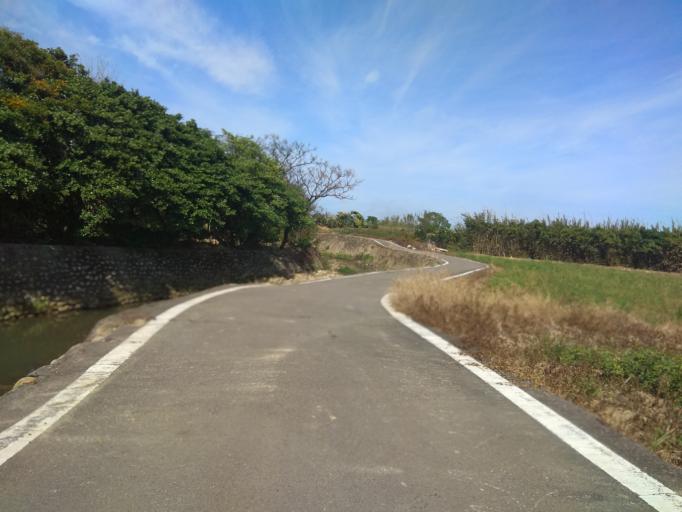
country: TW
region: Taiwan
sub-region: Hsinchu
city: Zhubei
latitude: 25.0204
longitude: 121.0663
